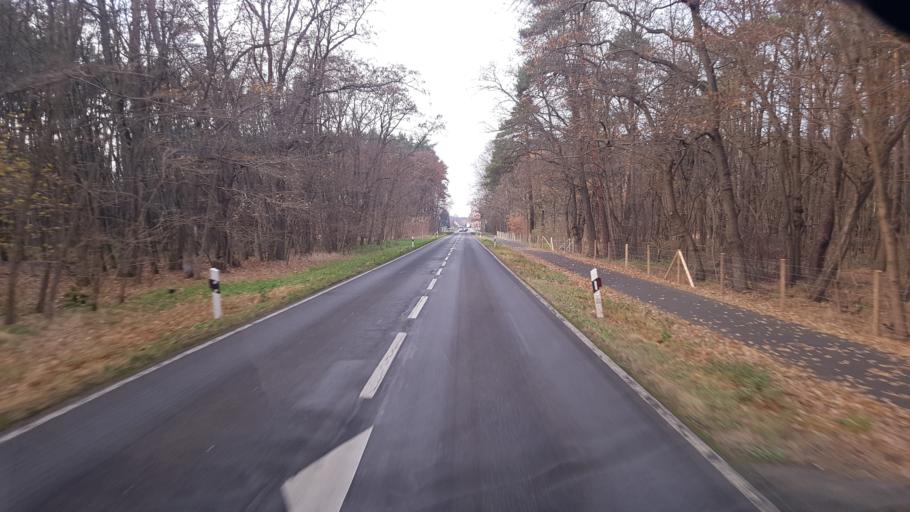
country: DE
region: Brandenburg
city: Ziltendorf
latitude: 52.1985
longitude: 14.6360
